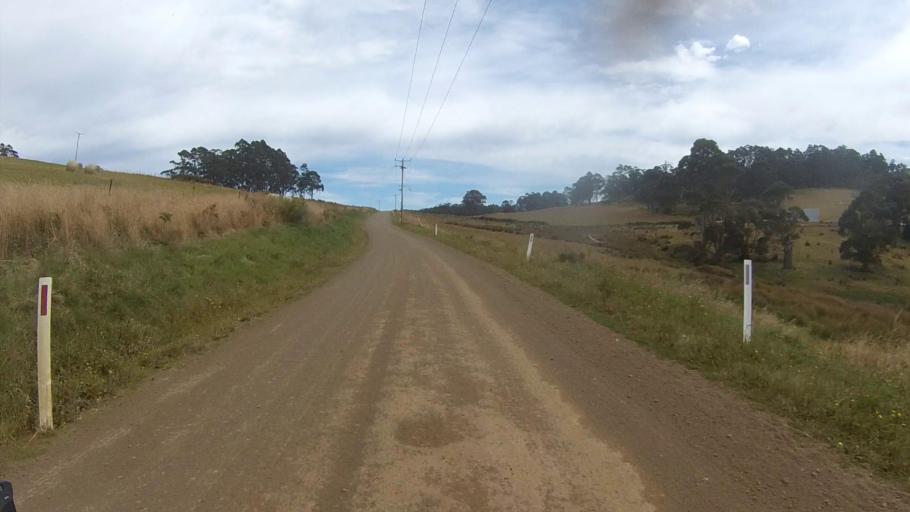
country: AU
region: Tasmania
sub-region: Sorell
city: Sorell
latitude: -42.7251
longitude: 147.7535
